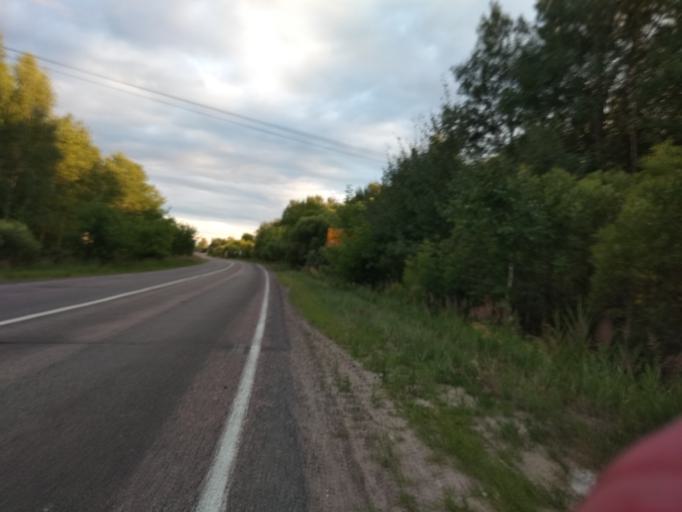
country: RU
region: Moskovskaya
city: Misheronskiy
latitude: 55.6045
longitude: 39.7085
